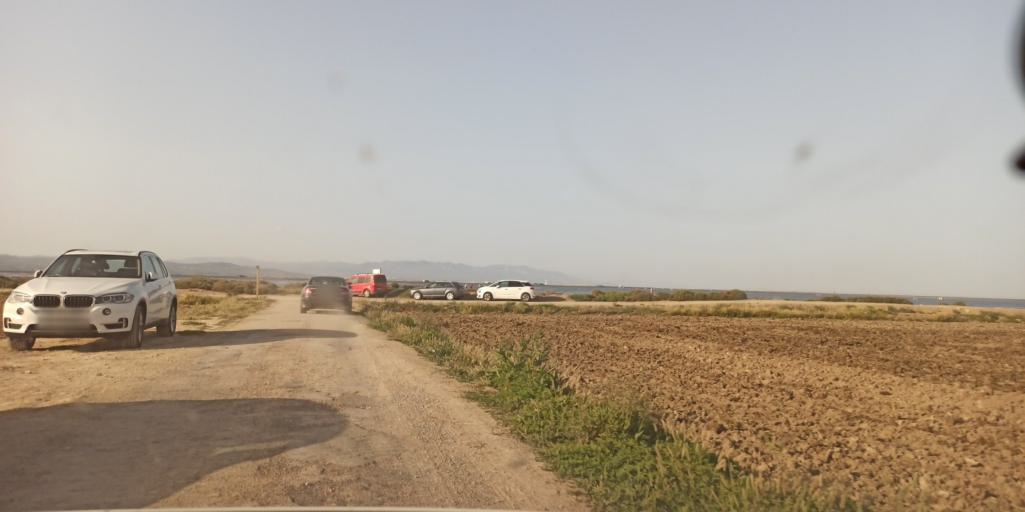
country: ES
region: Catalonia
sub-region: Provincia de Tarragona
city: Deltebre
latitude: 40.7624
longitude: 0.7544
